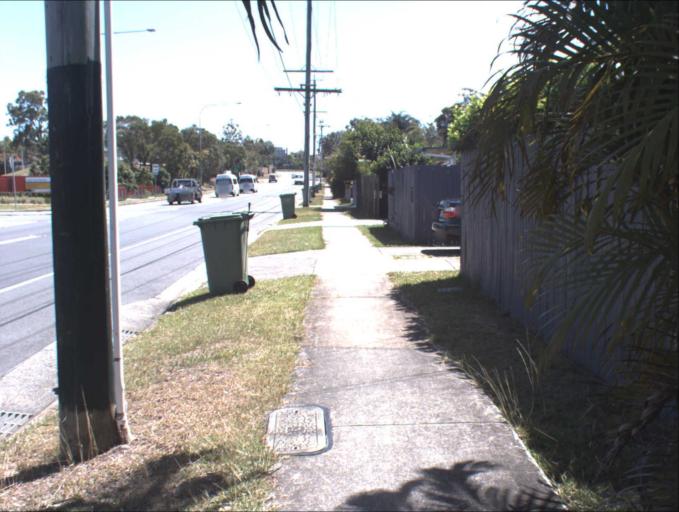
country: AU
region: Queensland
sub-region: Logan
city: Springwood
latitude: -27.6102
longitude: 153.1195
